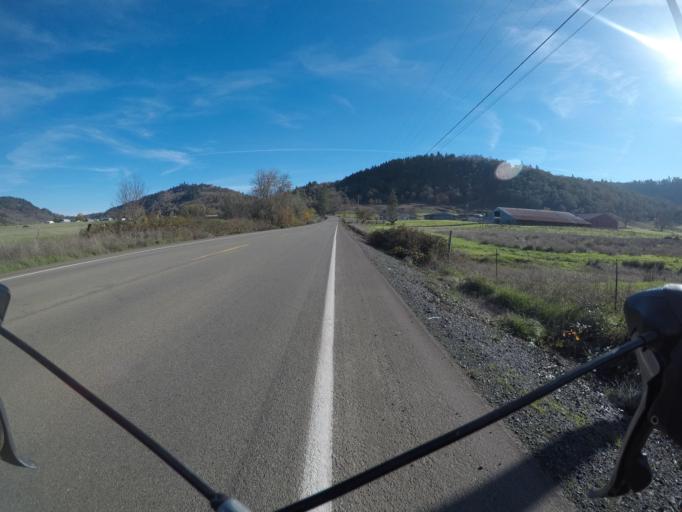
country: US
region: Oregon
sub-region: Douglas County
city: Winston
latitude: 43.1860
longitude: -123.4638
